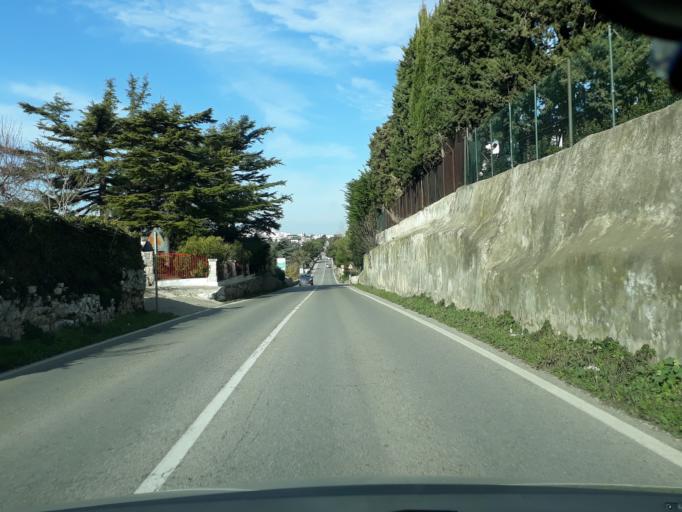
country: IT
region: Apulia
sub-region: Provincia di Taranto
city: Martina Franca
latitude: 40.7296
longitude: 17.3326
